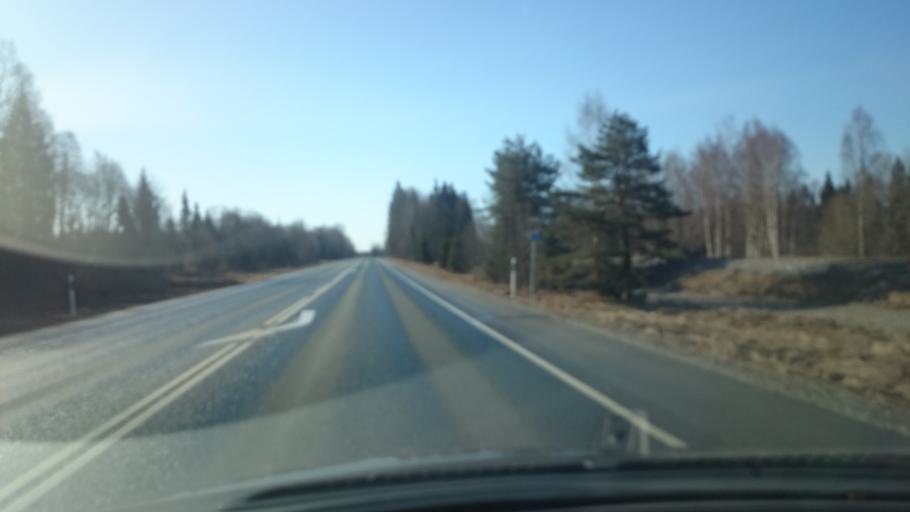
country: EE
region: Raplamaa
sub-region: Rapla vald
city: Rapla
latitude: 59.0483
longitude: 24.8377
